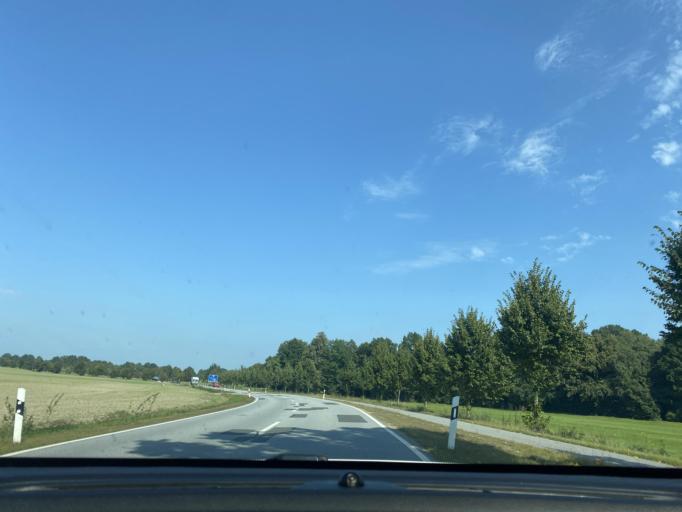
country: DE
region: Saxony
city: Reichenbach
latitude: 51.1977
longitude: 14.7581
